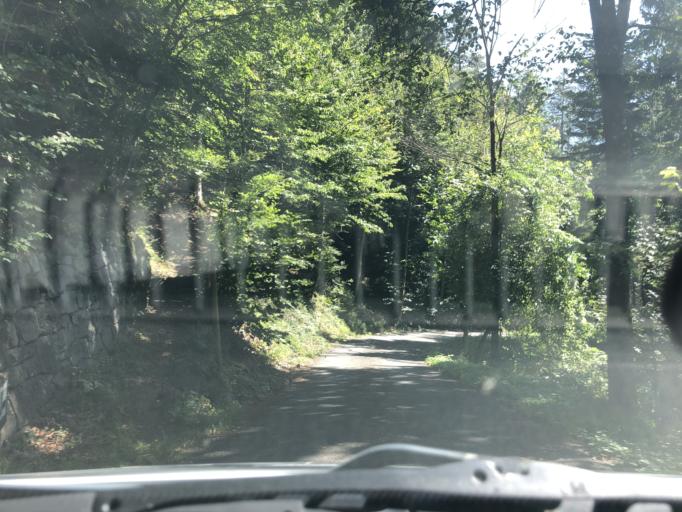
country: CH
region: Uri
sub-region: Uri
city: Altdorf
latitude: 46.8883
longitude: 8.6393
